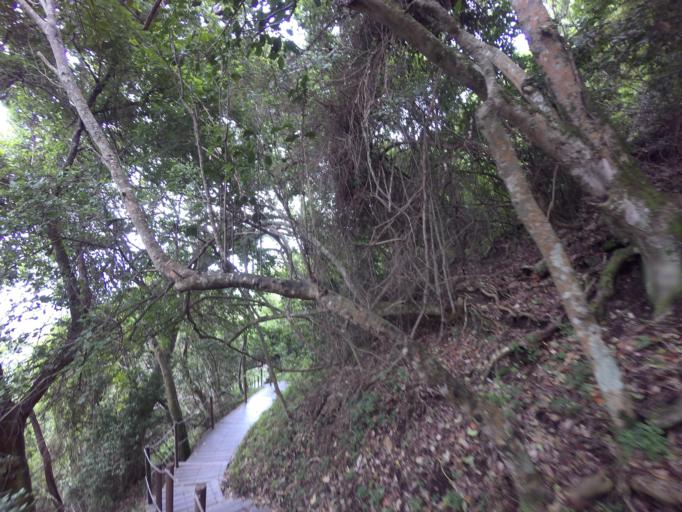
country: ZA
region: Eastern Cape
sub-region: Cacadu District Municipality
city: Kareedouw
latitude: -34.0206
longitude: 23.9000
